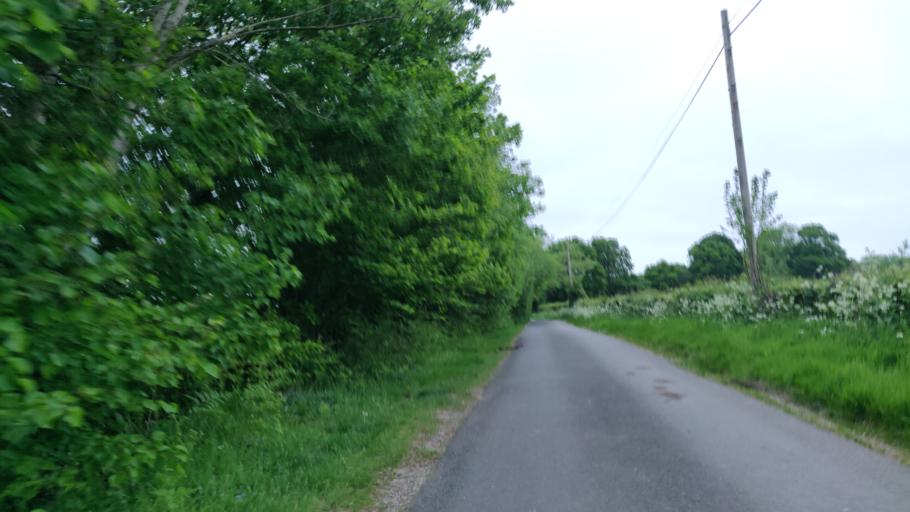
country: GB
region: England
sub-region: West Sussex
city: Southwater
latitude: 51.0290
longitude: -0.3343
